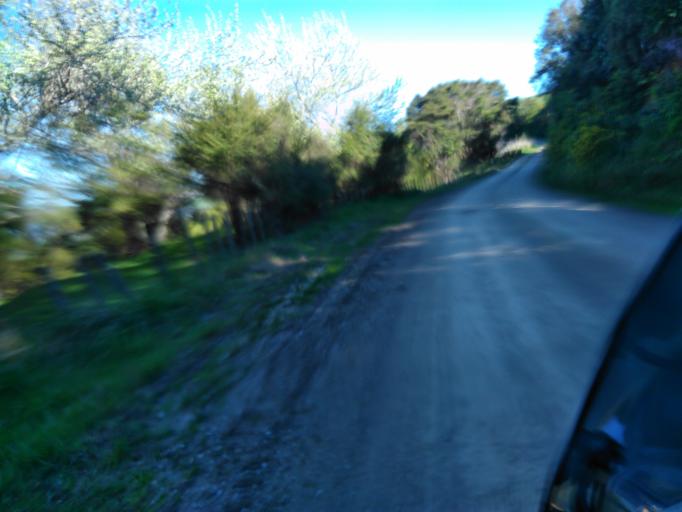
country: NZ
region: Gisborne
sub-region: Gisborne District
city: Gisborne
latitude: -38.3978
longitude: 177.6766
